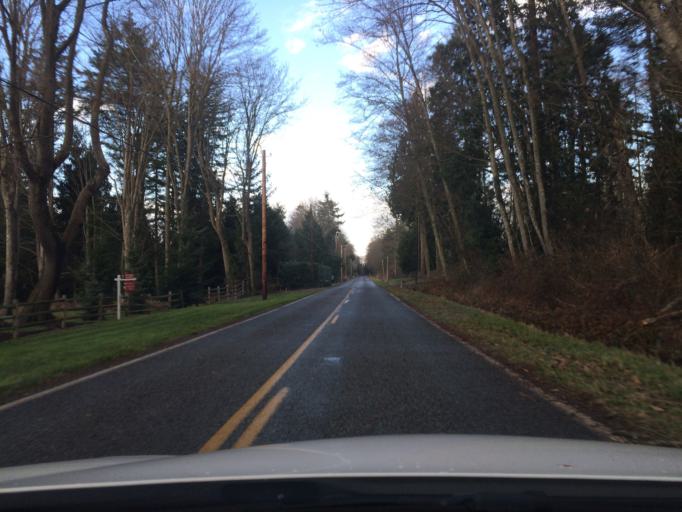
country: CA
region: British Columbia
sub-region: Greater Vancouver Regional District
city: White Rock
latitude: 48.9507
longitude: -122.8174
